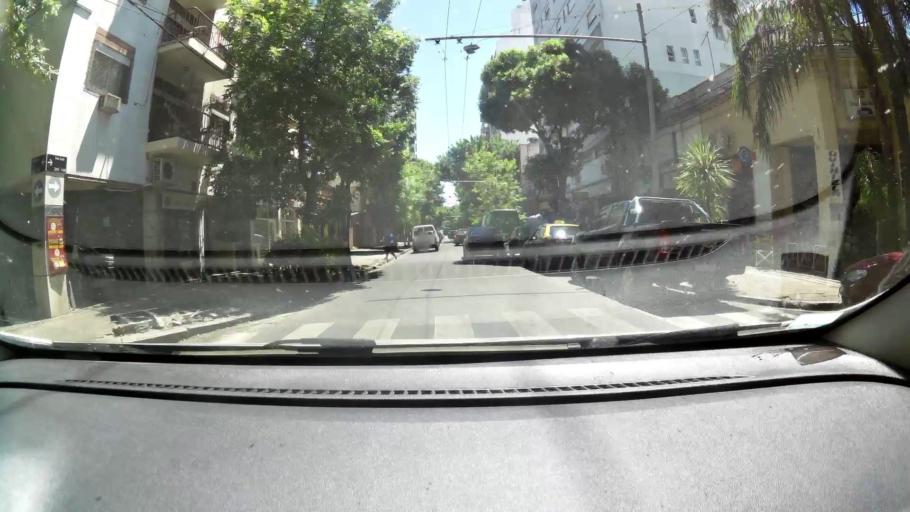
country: AR
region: Santa Fe
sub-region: Departamento de Rosario
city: Rosario
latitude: -32.9458
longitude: -60.6652
